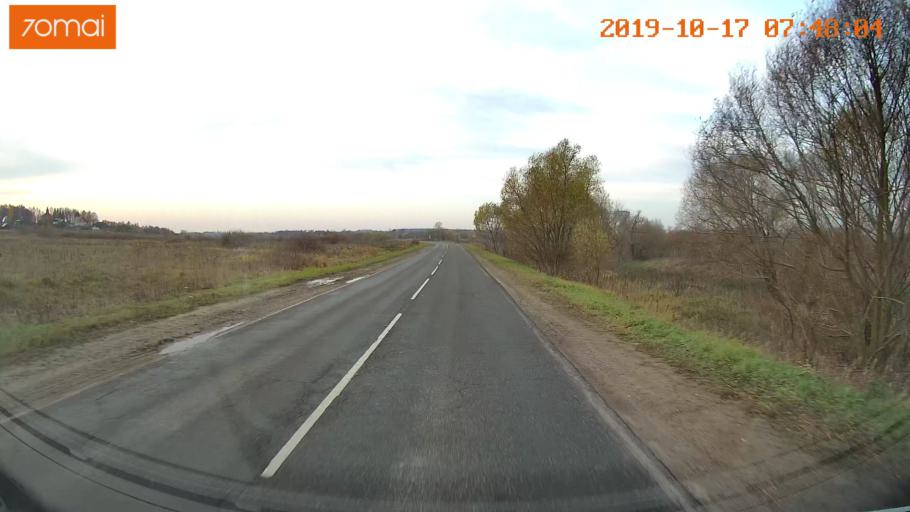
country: RU
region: Vladimir
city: Yur'yev-Pol'skiy
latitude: 56.4835
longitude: 39.6779
